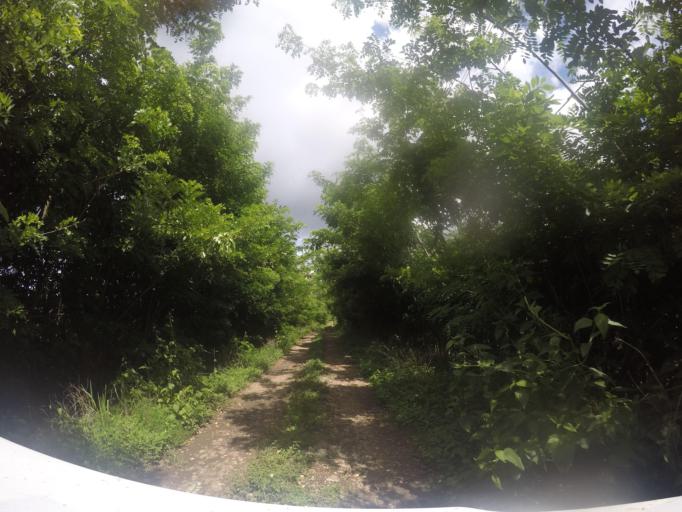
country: TL
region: Lautem
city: Lospalos
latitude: -8.4942
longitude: 127.0078
